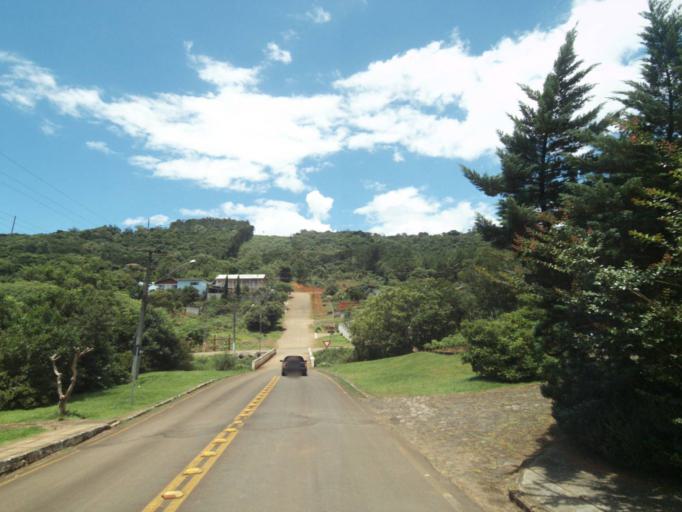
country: BR
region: Parana
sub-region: Uniao Da Vitoria
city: Uniao da Vitoria
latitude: -26.1609
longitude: -51.5536
